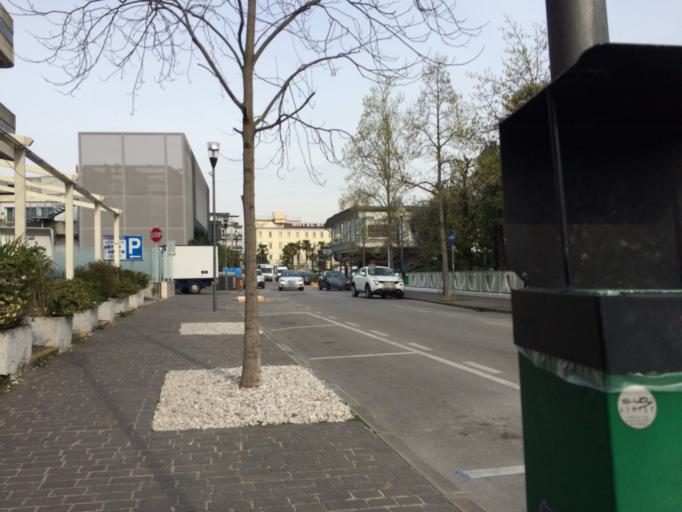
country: IT
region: Veneto
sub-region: Provincia di Padova
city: Abano Terme
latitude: 45.3537
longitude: 11.7848
